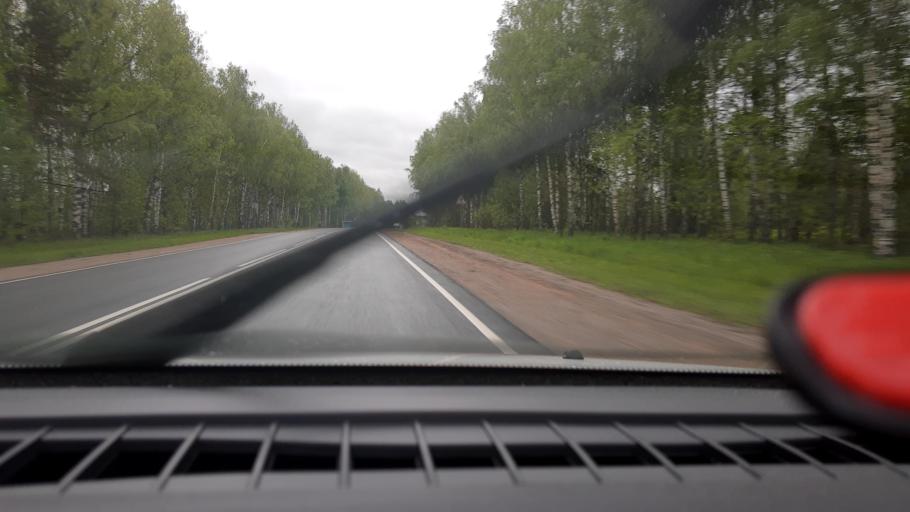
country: RU
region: Nizjnij Novgorod
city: Krasnyye Baki
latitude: 57.0560
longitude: 45.1364
